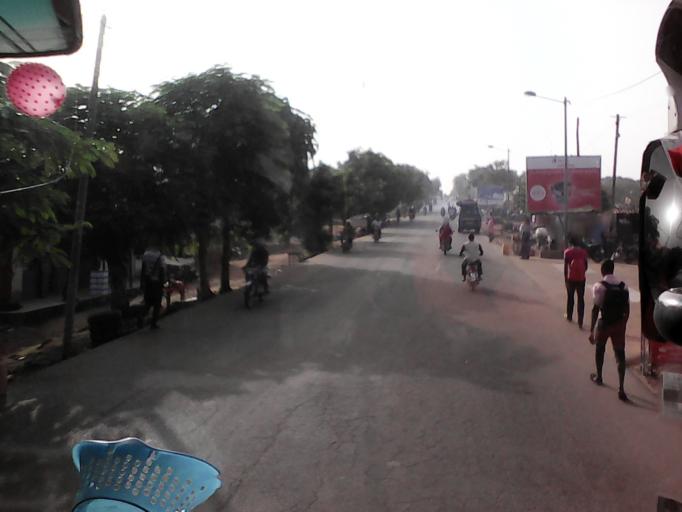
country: TG
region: Kara
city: Kara
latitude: 9.5336
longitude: 1.2001
